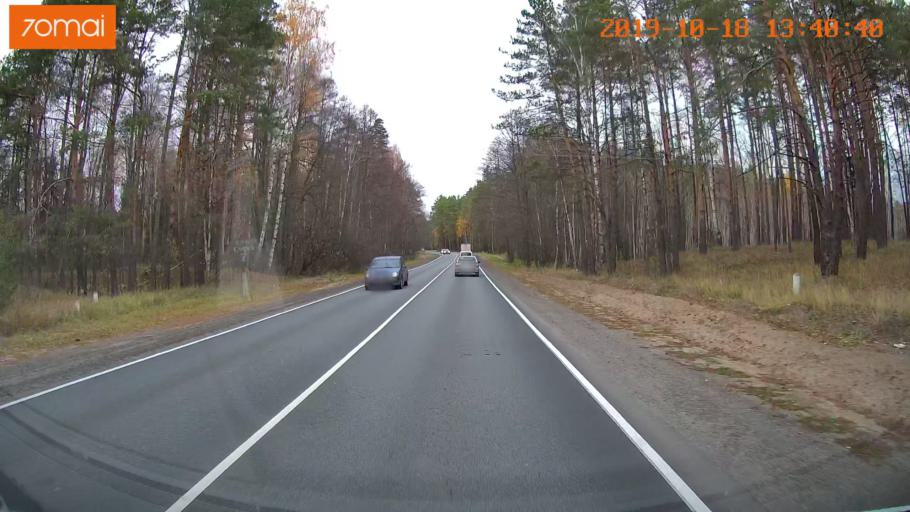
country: RU
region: Rjazan
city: Solotcha
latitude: 54.9125
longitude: 39.9978
